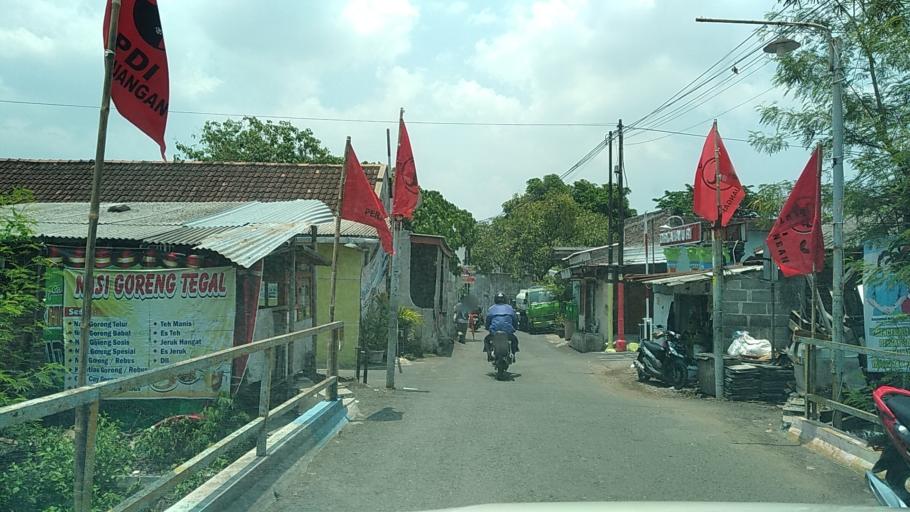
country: ID
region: Central Java
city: Semarang
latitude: -7.0030
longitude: 110.4410
